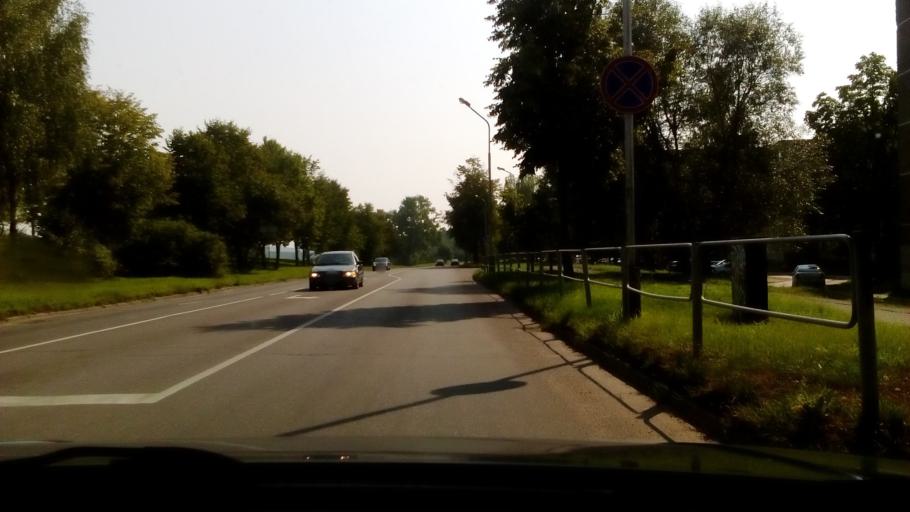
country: LT
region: Alytaus apskritis
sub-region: Alytus
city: Alytus
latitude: 54.4114
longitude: 24.0236
